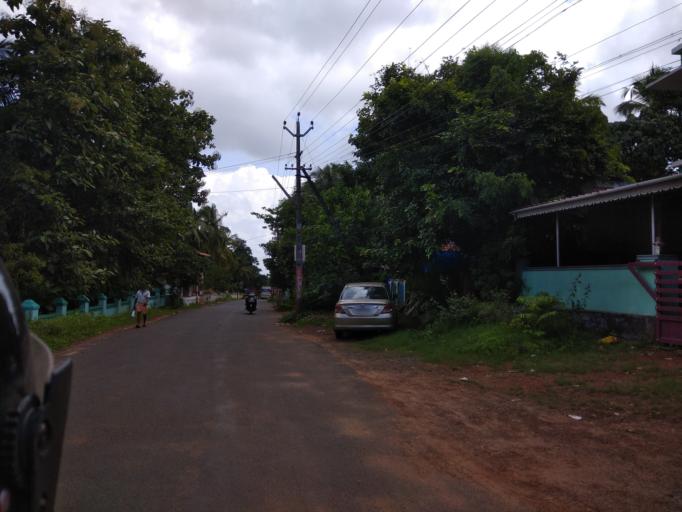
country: IN
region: Kerala
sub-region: Thrissur District
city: Avanoor
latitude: 10.5450
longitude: 76.1471
